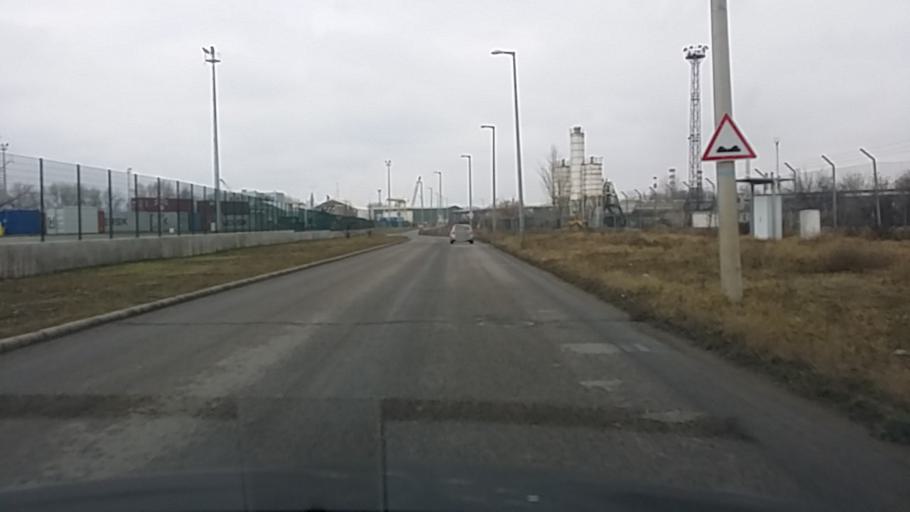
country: HU
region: Budapest
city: Budapest XXII. keruelet
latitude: 47.4184
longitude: 19.0515
